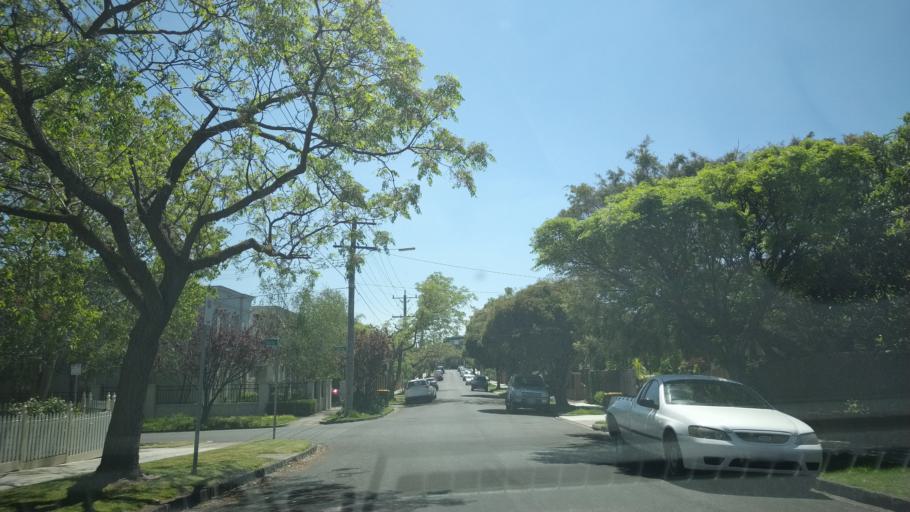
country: AU
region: Victoria
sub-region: Glen Eira
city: Caulfield South
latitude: -37.8901
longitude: 145.0314
